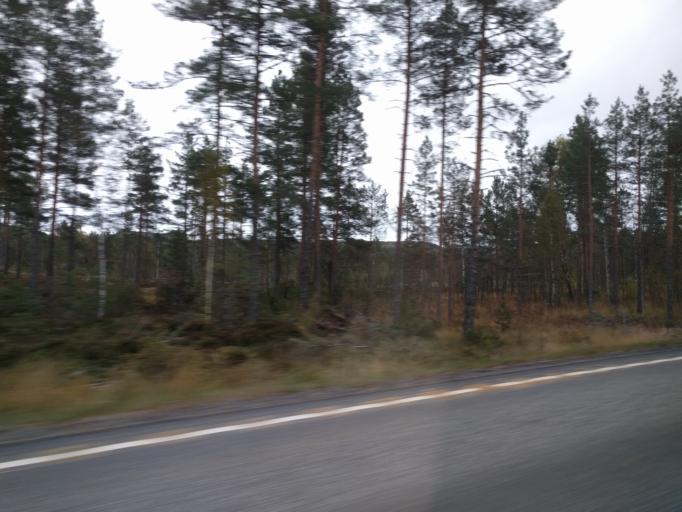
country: NO
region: Aust-Agder
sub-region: Evje og Hornnes
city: Evje
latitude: 58.5278
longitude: 7.7794
